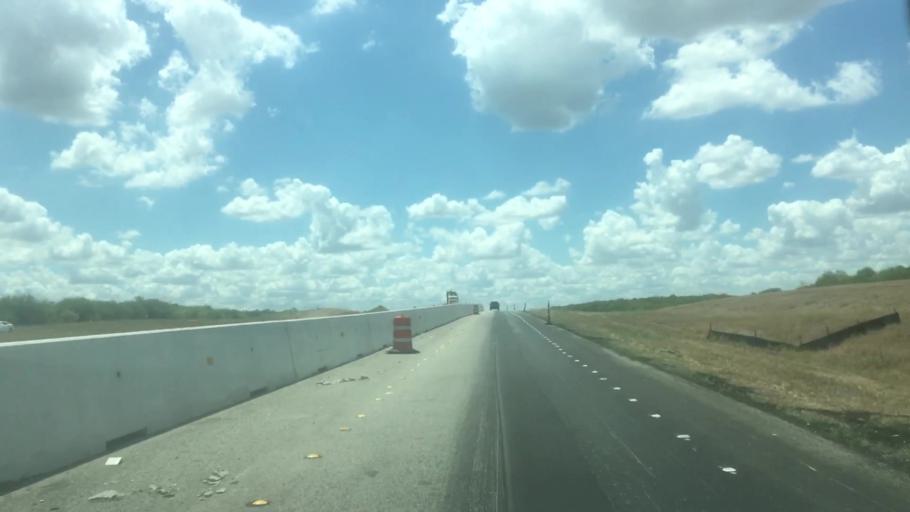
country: US
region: Texas
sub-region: Caldwell County
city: Martindale
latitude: 29.8251
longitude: -97.7487
